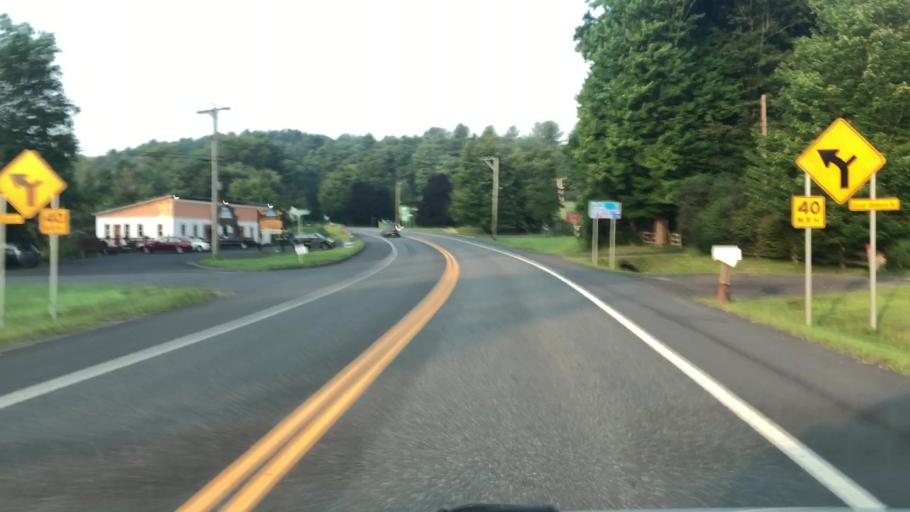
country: US
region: Massachusetts
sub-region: Franklin County
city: Shelburne
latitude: 42.6112
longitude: -72.6698
